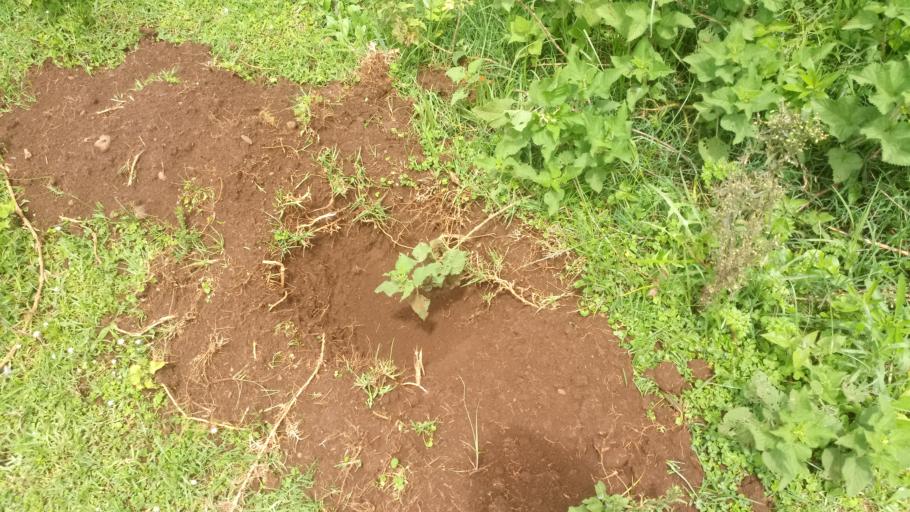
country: KE
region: Kirinyaga
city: Keruguya
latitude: -0.3952
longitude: 37.1614
